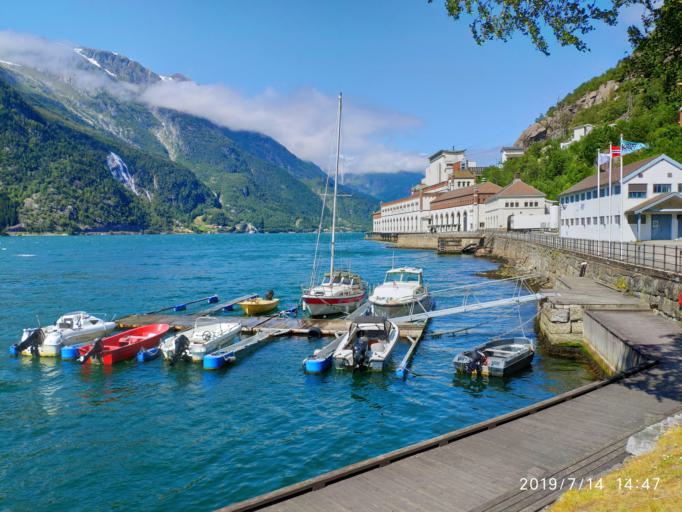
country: NO
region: Hordaland
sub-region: Odda
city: Odda
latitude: 60.1195
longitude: 6.5564
